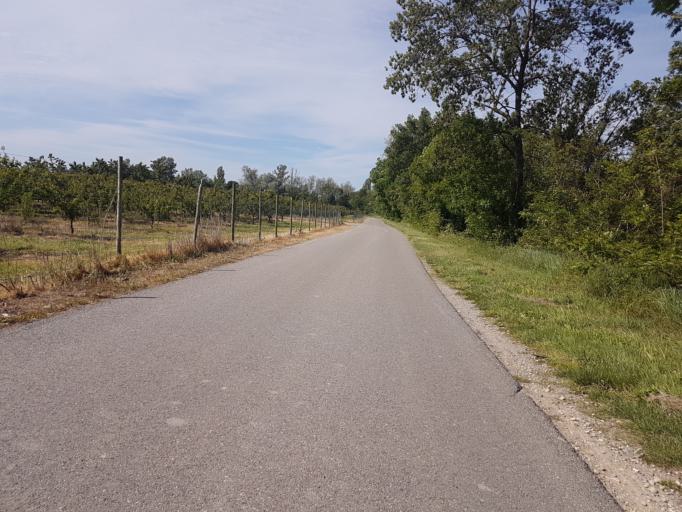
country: FR
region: Rhone-Alpes
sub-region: Departement de l'Ardeche
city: La Voulte-sur-Rhone
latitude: 44.7902
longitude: 4.7787
